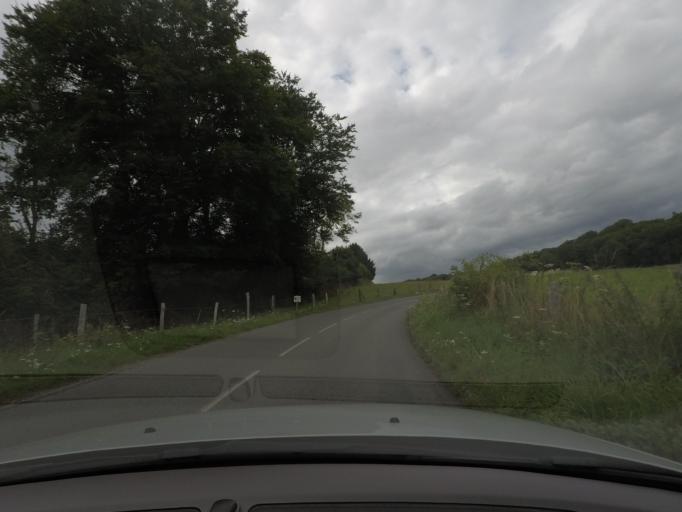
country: FR
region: Haute-Normandie
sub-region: Departement de l'Eure
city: Les Andelys
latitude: 49.2835
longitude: 1.3480
